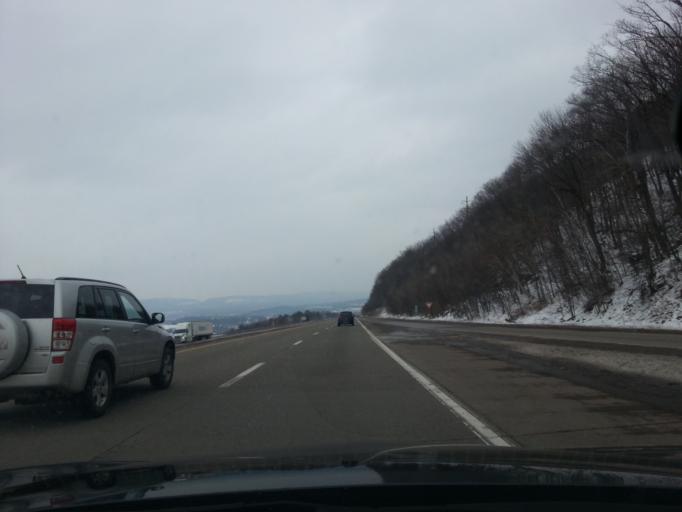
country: US
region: Pennsylvania
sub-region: Luzerne County
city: Conyngham
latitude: 40.9848
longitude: -76.0339
